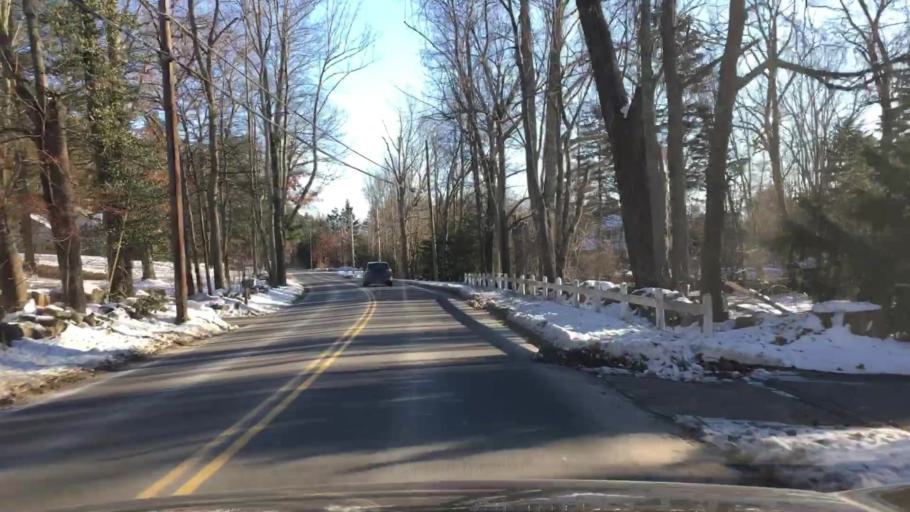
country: US
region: New Hampshire
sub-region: Hillsborough County
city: Milford
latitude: 42.8323
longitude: -71.5916
